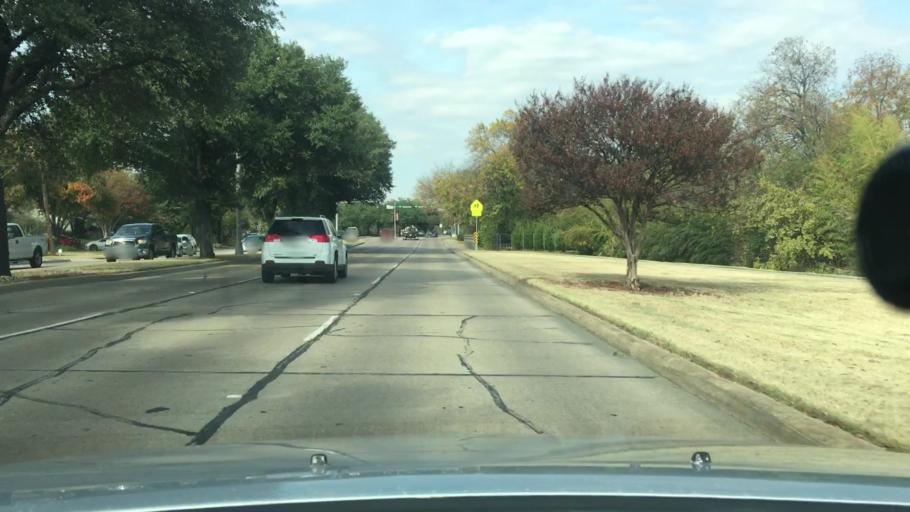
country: US
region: Texas
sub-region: Denton County
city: Denton
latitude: 33.2238
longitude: -97.1369
